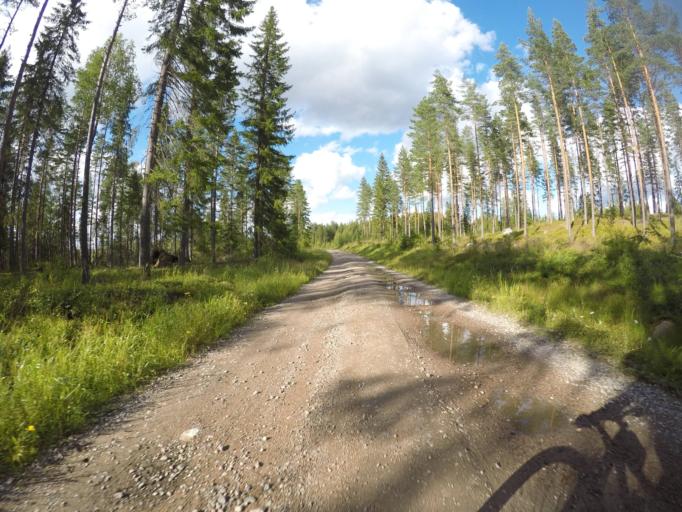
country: SE
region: OErebro
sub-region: Hallefors Kommun
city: Haellefors
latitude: 59.9248
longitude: 14.5668
